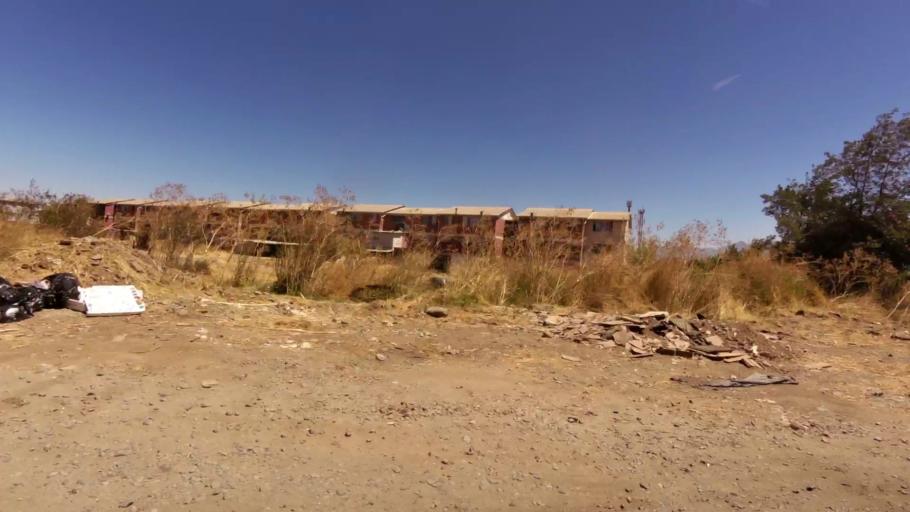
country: CL
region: O'Higgins
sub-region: Provincia de Cachapoal
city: Rancagua
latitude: -34.1511
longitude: -70.7166
